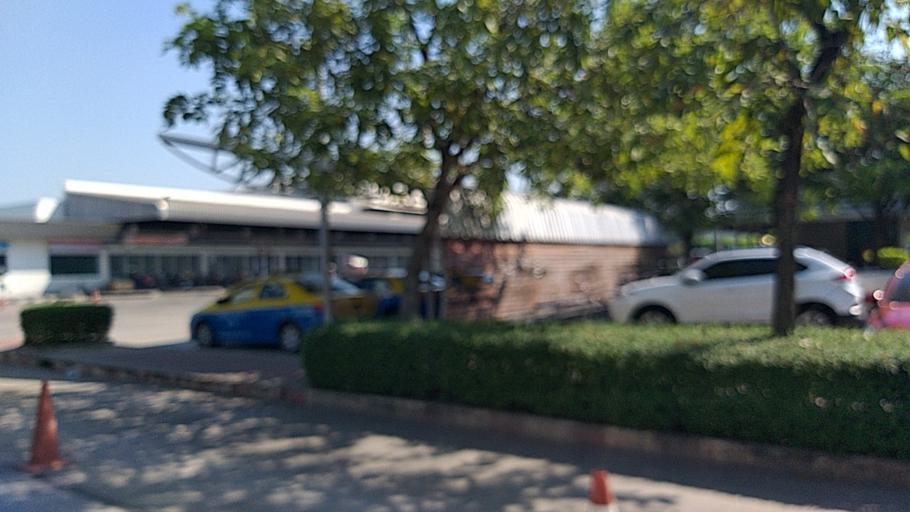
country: TH
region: Nakhon Ratchasima
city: Nakhon Ratchasima
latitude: 14.9881
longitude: 102.0942
